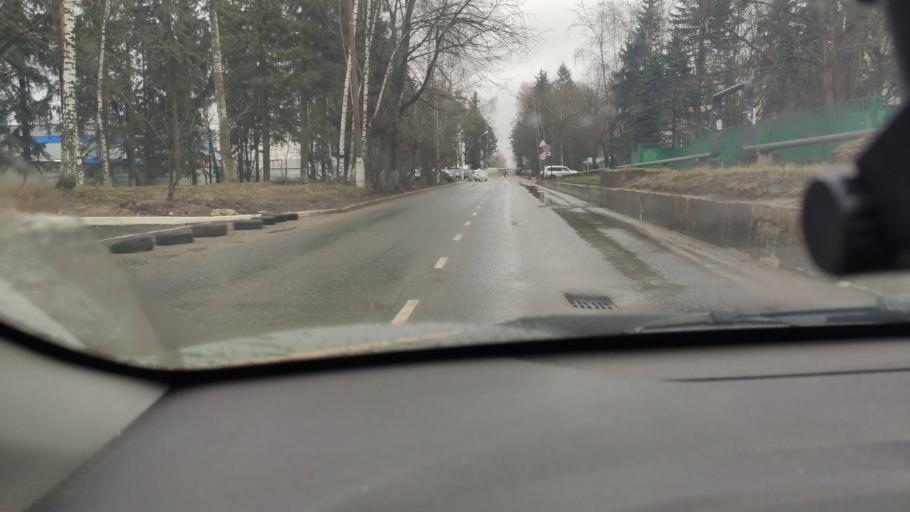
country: RU
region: Moskovskaya
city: Selyatino
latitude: 55.5160
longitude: 36.9733
